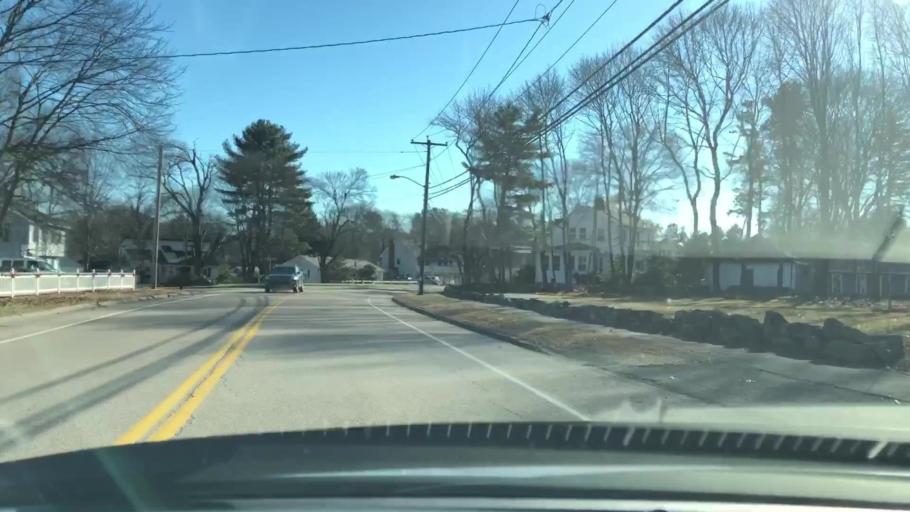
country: US
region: Massachusetts
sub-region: Norfolk County
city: Walpole
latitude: 42.1704
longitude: -71.2398
